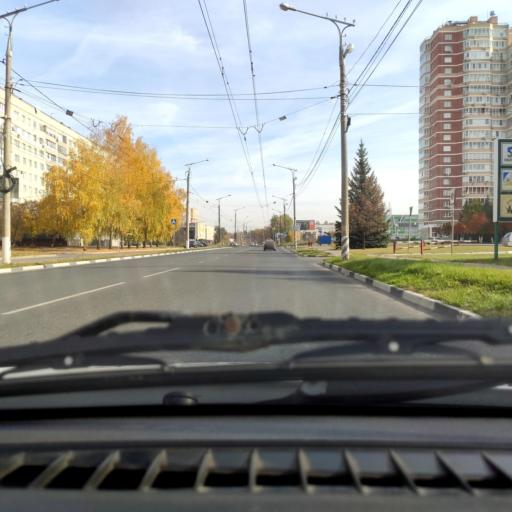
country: RU
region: Samara
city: Tol'yatti
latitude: 53.5005
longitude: 49.4181
